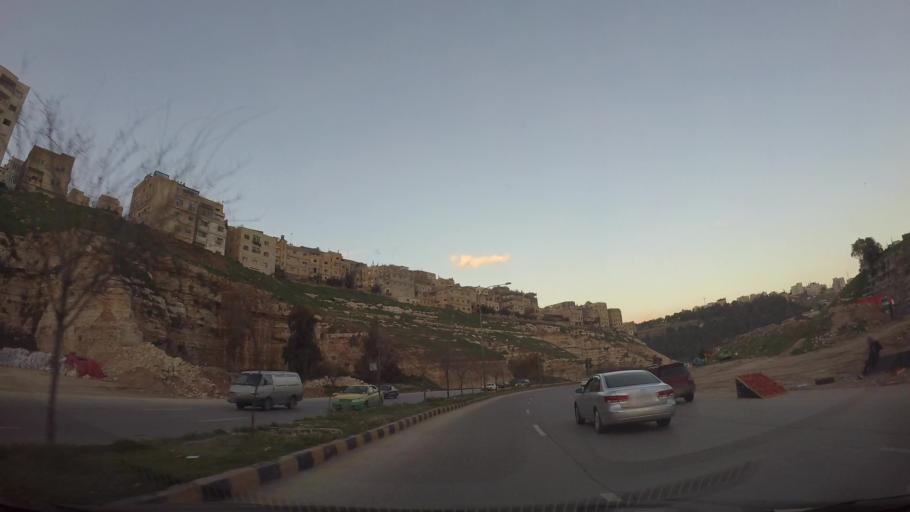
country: JO
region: Amman
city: Al Quwaysimah
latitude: 31.9275
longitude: 35.9127
